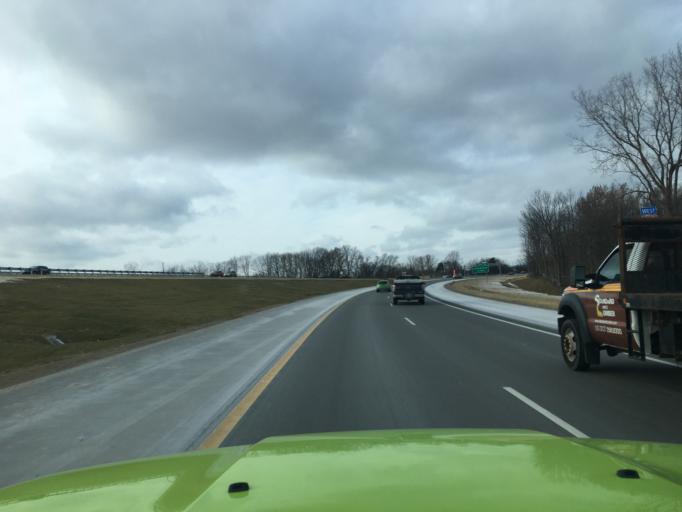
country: US
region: Michigan
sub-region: Kent County
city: East Grand Rapids
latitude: 42.9770
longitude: -85.6026
